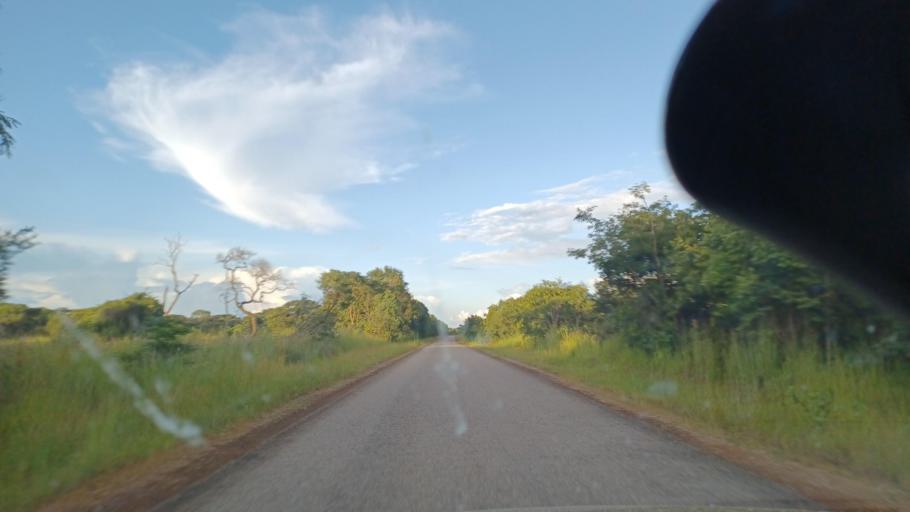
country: ZM
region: North-Western
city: Kalengwa
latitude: -13.0851
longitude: 25.2877
